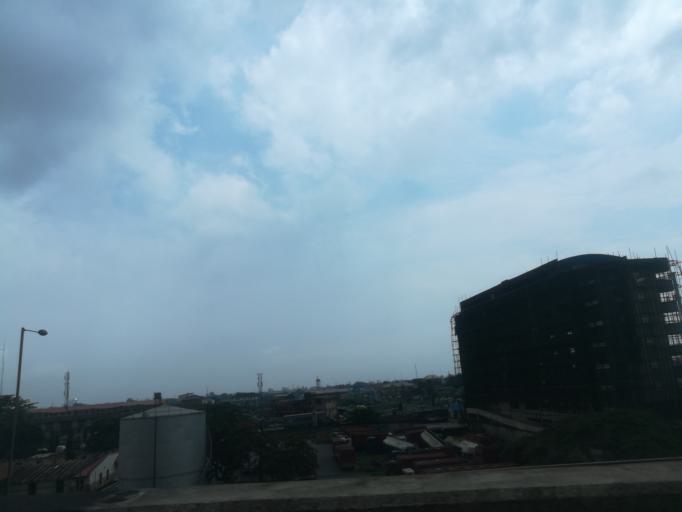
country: NG
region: Lagos
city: Surulere
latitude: 6.4827
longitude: 3.3666
